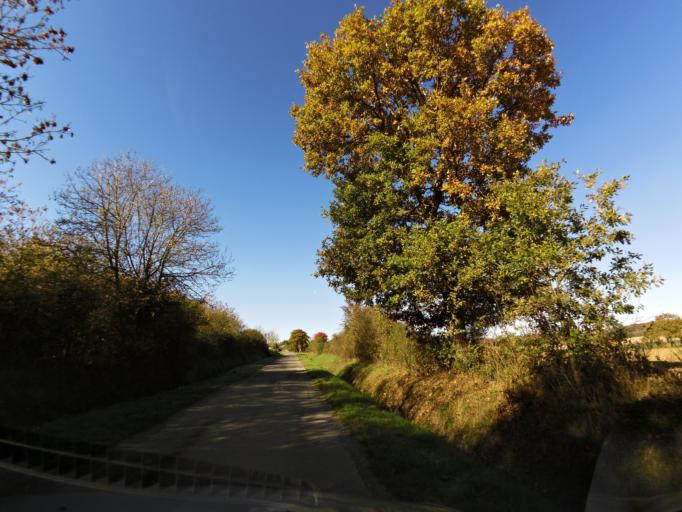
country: FR
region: Brittany
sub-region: Departement d'Ille-et-Vilaine
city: Bain-de-Bretagne
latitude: 47.8574
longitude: -1.7073
